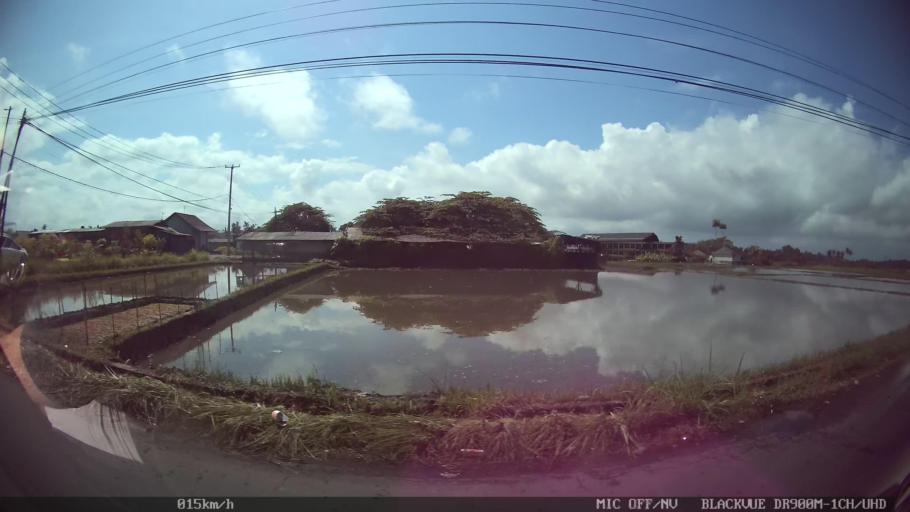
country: ID
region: Bali
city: Banjar Sedang
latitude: -8.5608
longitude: 115.2658
